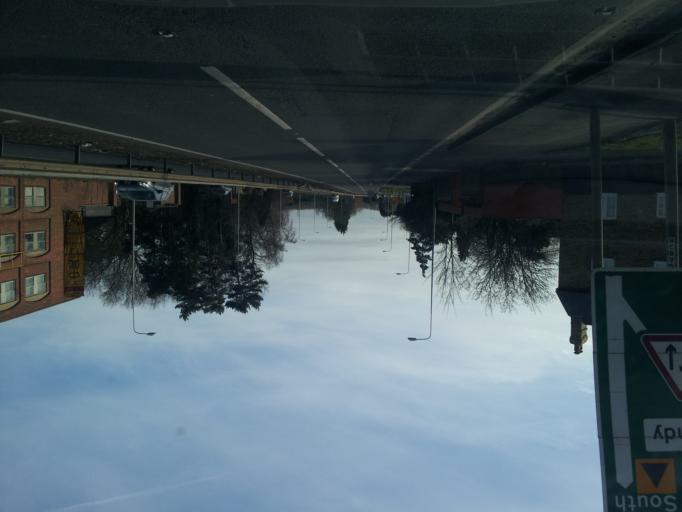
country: GB
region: England
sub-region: Central Bedfordshire
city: Sandy
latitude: 52.1350
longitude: -0.2992
